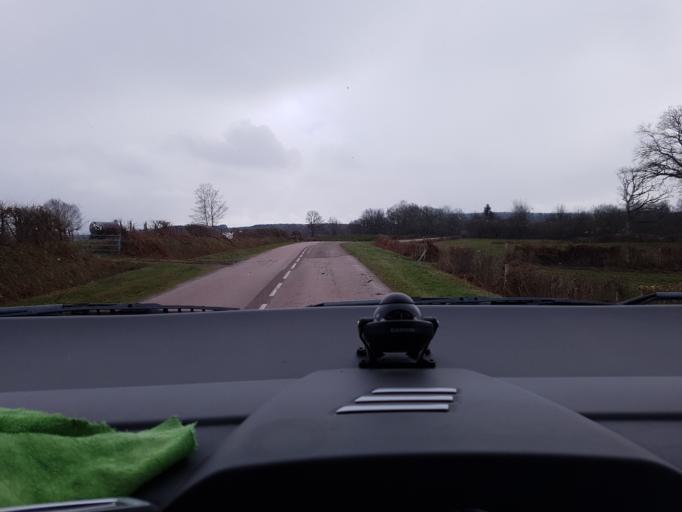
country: FR
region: Bourgogne
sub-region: Departement de la Cote-d'Or
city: Saulieu
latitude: 47.2662
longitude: 4.0290
